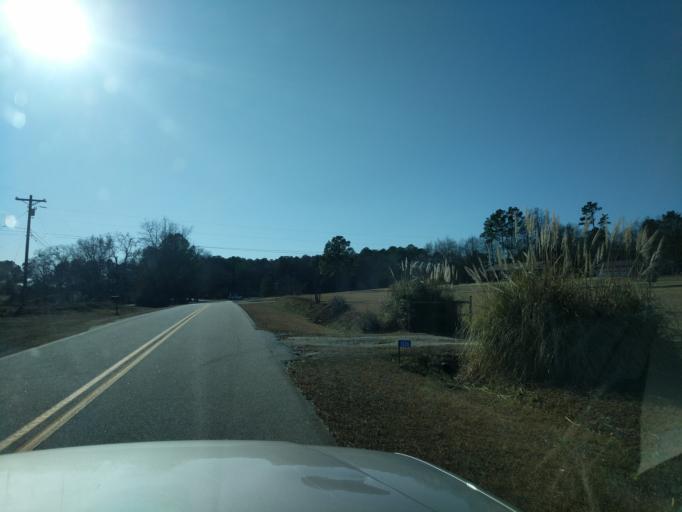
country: US
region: Georgia
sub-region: Hart County
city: Hartwell
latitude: 34.3312
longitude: -82.8709
